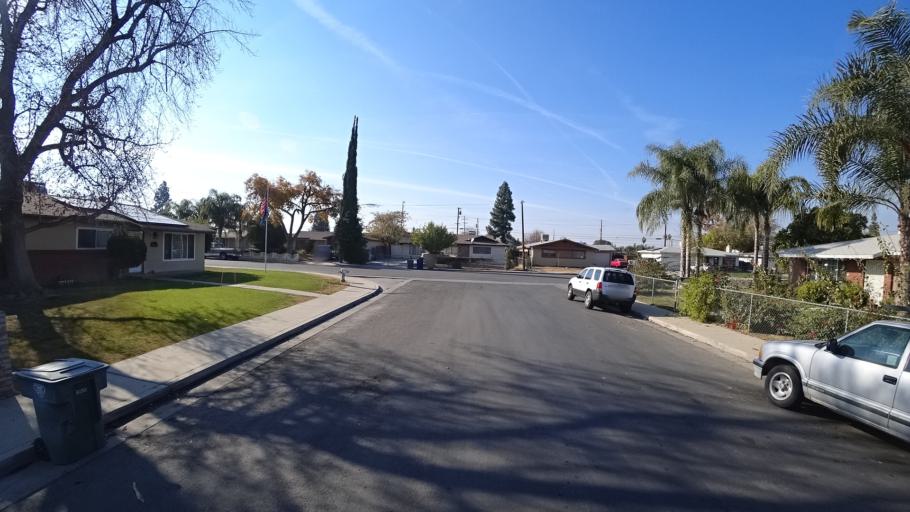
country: US
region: California
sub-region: Kern County
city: Bakersfield
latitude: 35.3200
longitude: -119.0200
